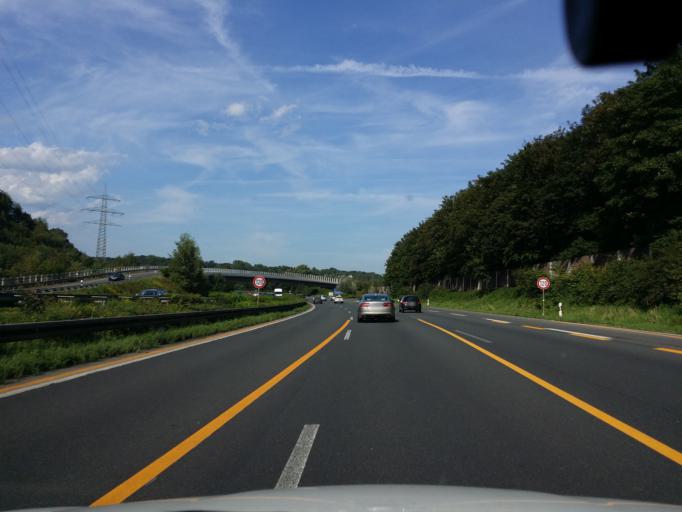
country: DE
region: North Rhine-Westphalia
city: Lohmar
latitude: 50.8482
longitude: 7.2122
